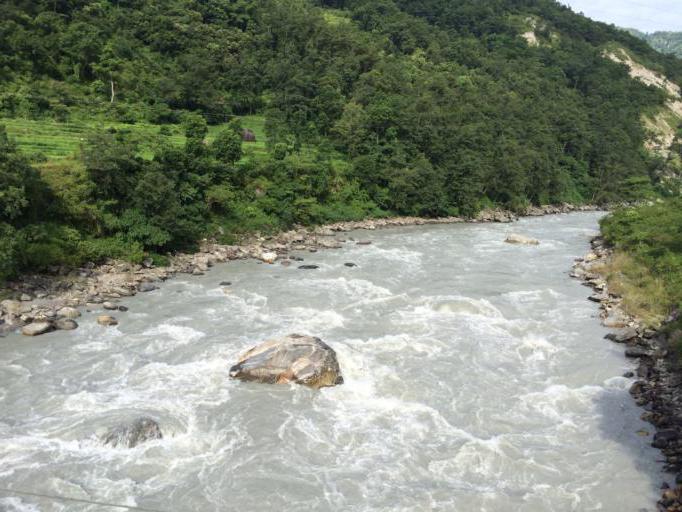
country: NP
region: Western Region
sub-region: Gandaki Zone
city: Khudi
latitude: 28.2540
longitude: 84.3711
